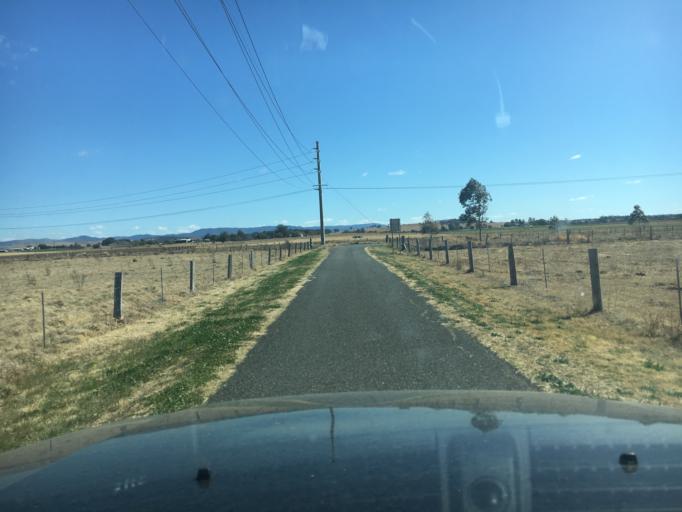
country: AU
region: New South Wales
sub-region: Singleton
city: Singleton
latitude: -32.5899
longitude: 151.1674
